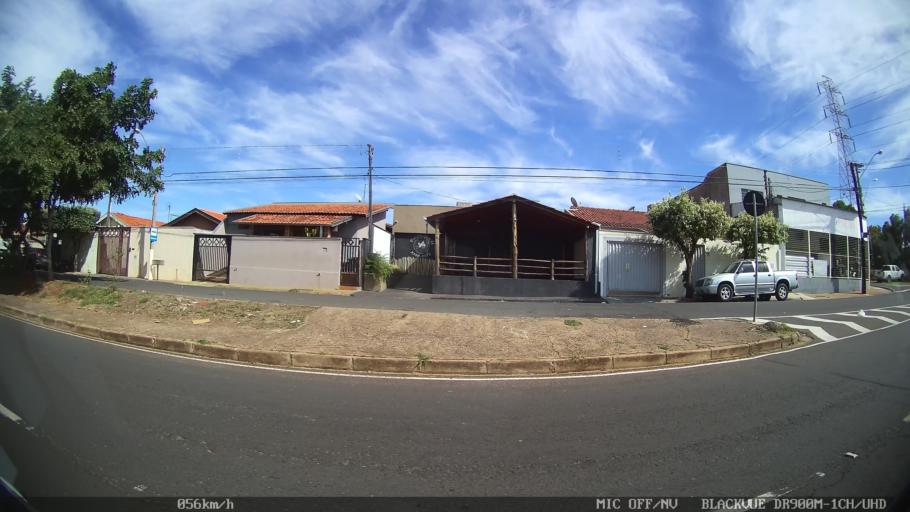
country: BR
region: Sao Paulo
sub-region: Sao Jose Do Rio Preto
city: Sao Jose do Rio Preto
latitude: -20.8329
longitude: -49.3495
